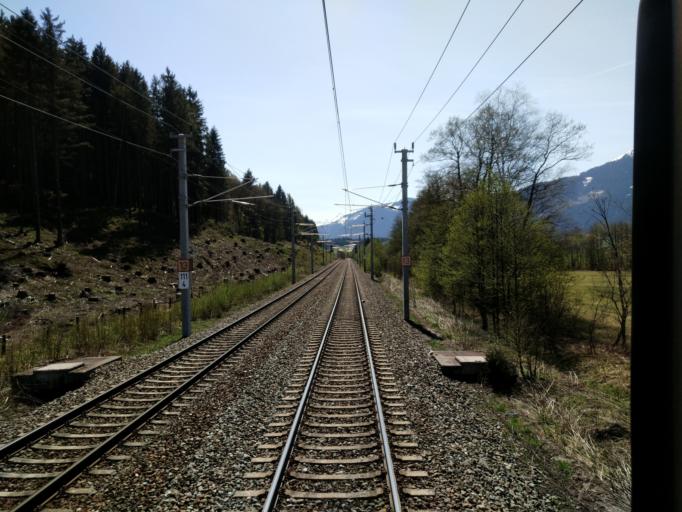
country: AT
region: Salzburg
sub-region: Politischer Bezirk Zell am See
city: Saalfelden am Steinernen Meer
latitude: 47.4185
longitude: 12.8308
